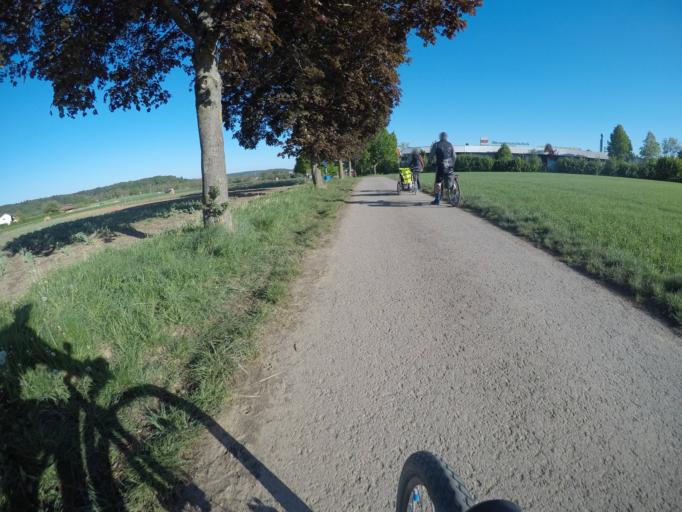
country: DE
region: Baden-Wuerttemberg
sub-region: Regierungsbezirk Stuttgart
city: Renningen
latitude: 48.7814
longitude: 8.9330
